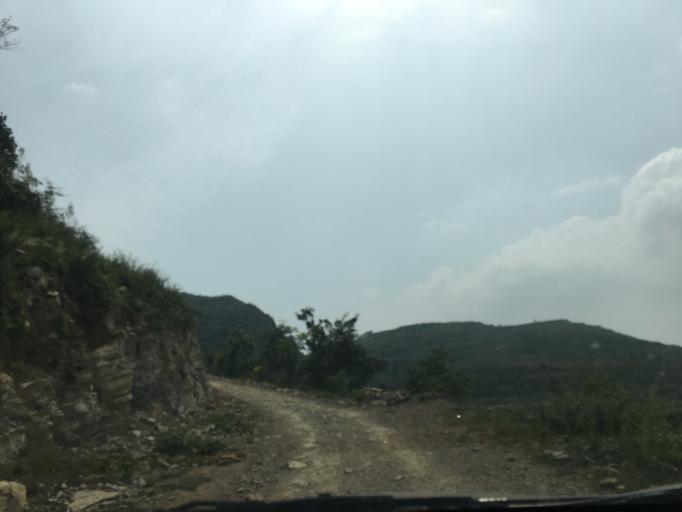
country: CN
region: Guizhou Sheng
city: Anshun
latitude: 25.5993
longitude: 105.6637
